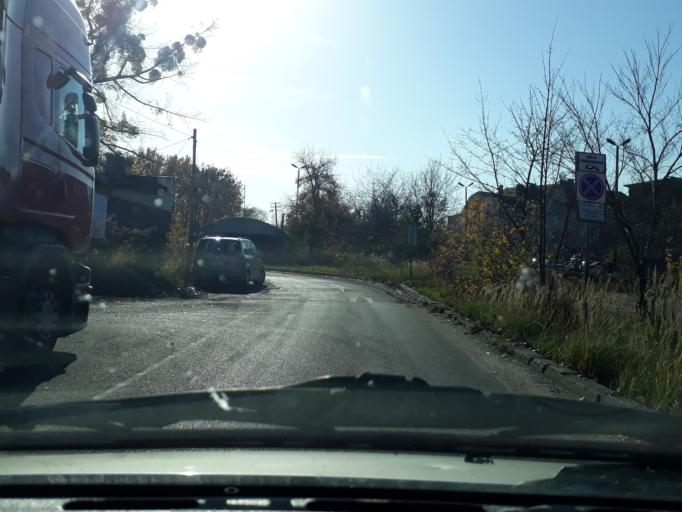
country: PL
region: Silesian Voivodeship
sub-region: Powiat tarnogorski
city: Tarnowskie Gory
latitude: 50.4425
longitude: 18.8628
